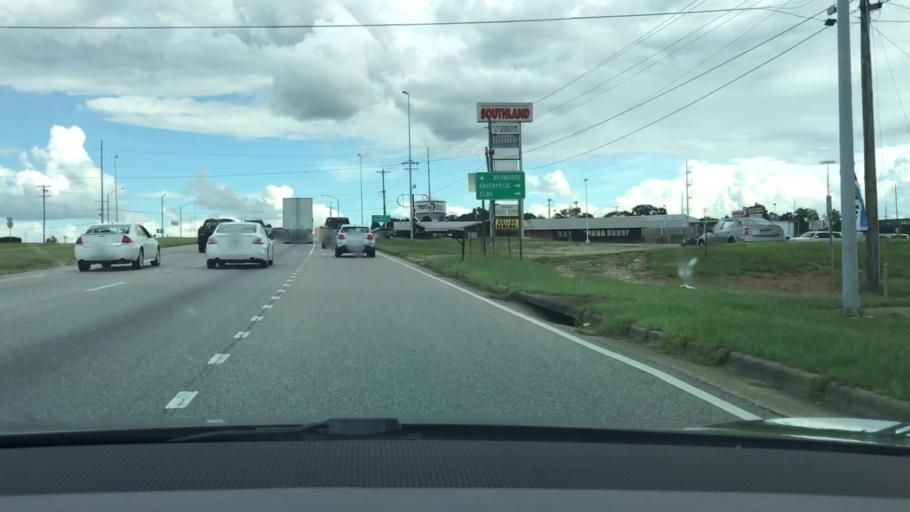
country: US
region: Alabama
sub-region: Pike County
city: Troy
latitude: 31.7864
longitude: -85.9666
